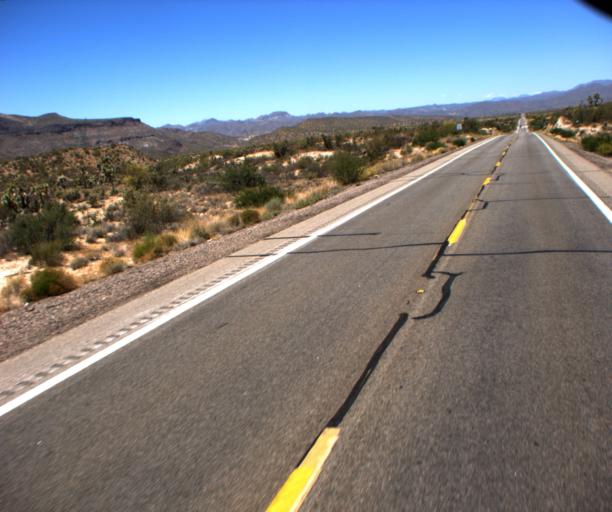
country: US
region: Arizona
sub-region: Yavapai County
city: Bagdad
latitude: 34.3123
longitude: -113.1281
